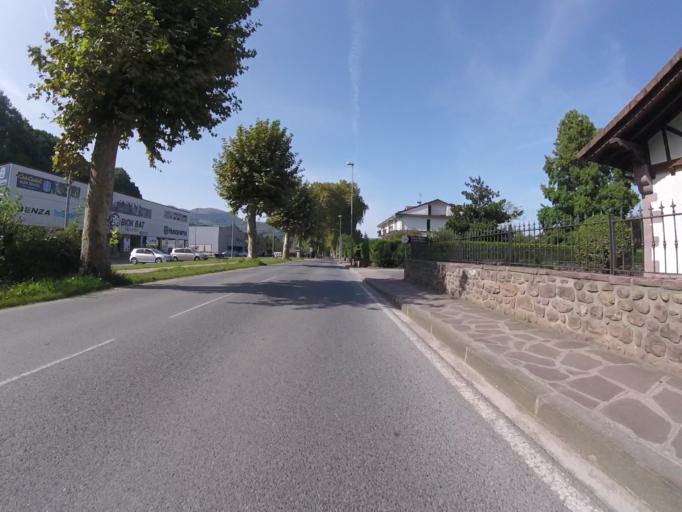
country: ES
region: Navarre
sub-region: Provincia de Navarra
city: Zugarramurdi
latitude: 43.1395
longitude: -1.5249
